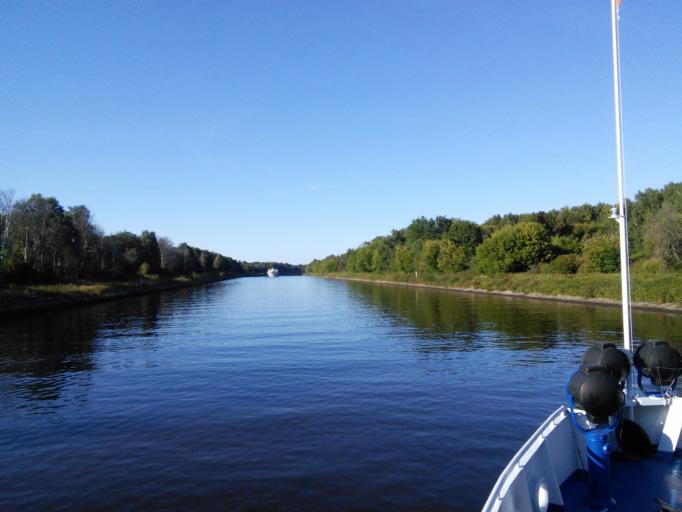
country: RU
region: Moskovskaya
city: Yakhroma
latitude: 56.3078
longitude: 37.4896
